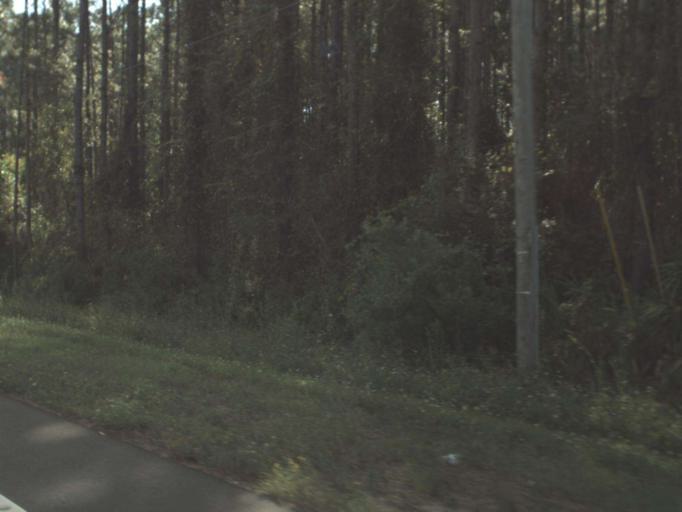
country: US
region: Florida
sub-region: Gulf County
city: Port Saint Joe
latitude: 29.8359
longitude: -85.2746
